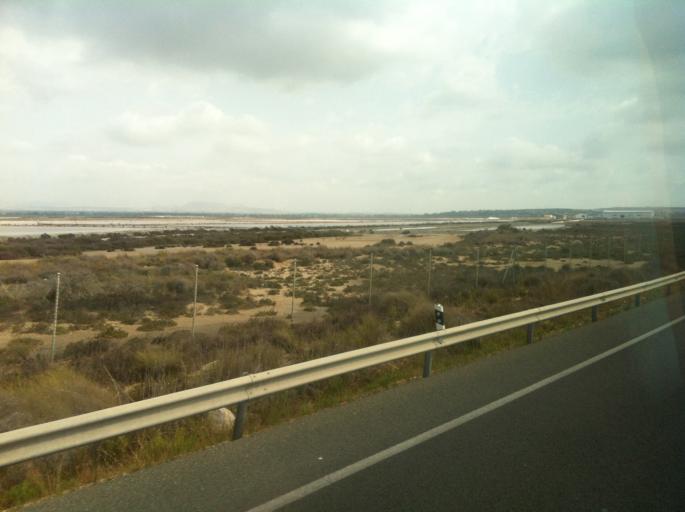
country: ES
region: Valencia
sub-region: Provincia de Alicante
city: Santa Pola
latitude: 38.1863
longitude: -0.6031
